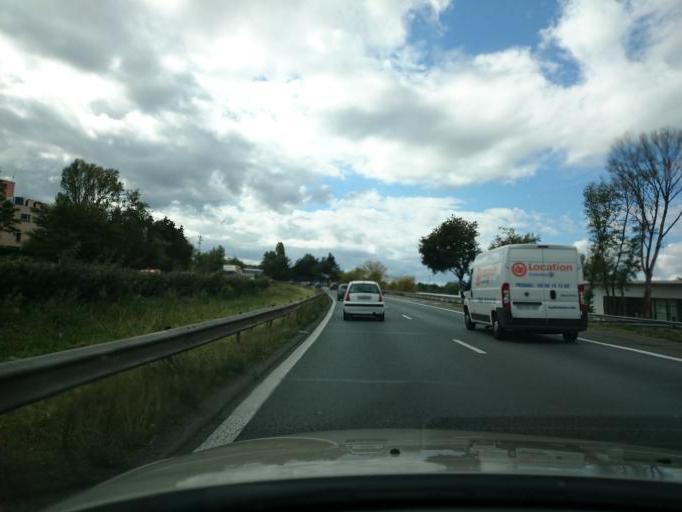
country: FR
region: Aquitaine
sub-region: Departement de la Gironde
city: Bruges
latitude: 44.8901
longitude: -0.6144
